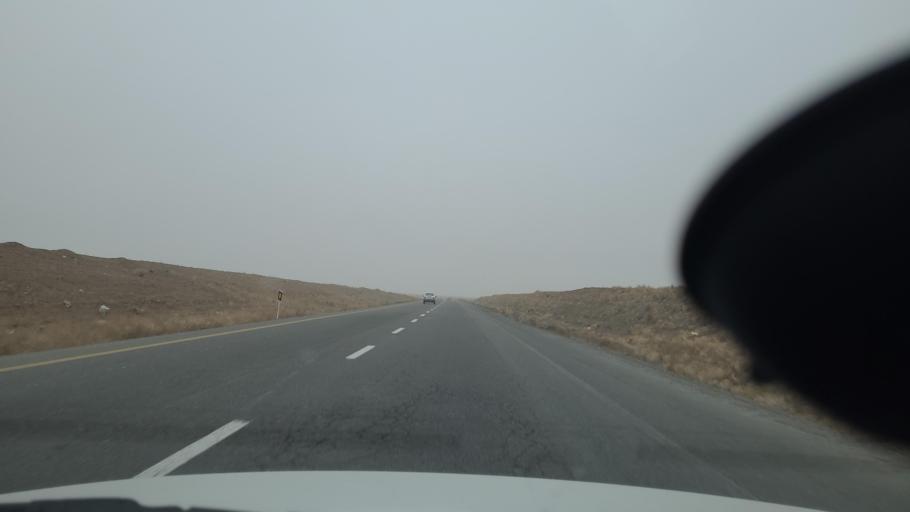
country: IR
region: Razavi Khorasan
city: Fariman
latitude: 35.8543
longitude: 59.7556
